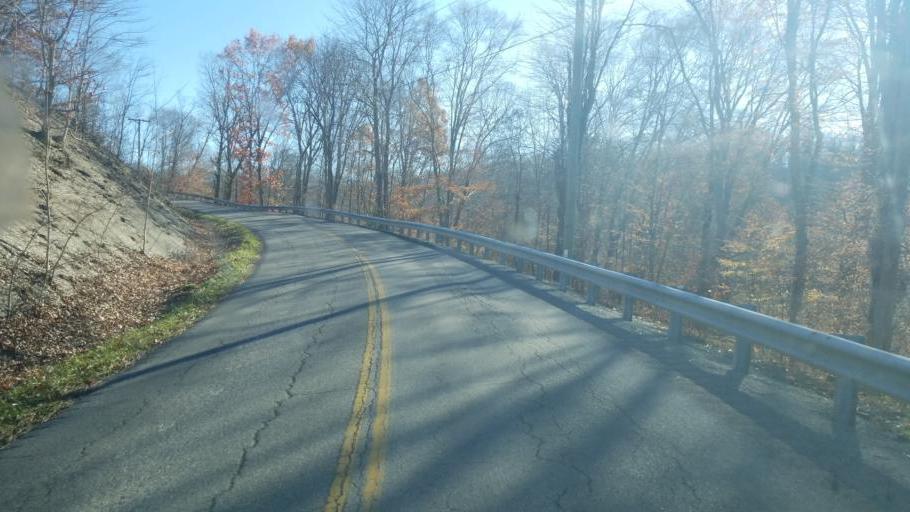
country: US
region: Kentucky
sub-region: Fleming County
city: Flemingsburg
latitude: 38.4651
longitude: -83.5348
